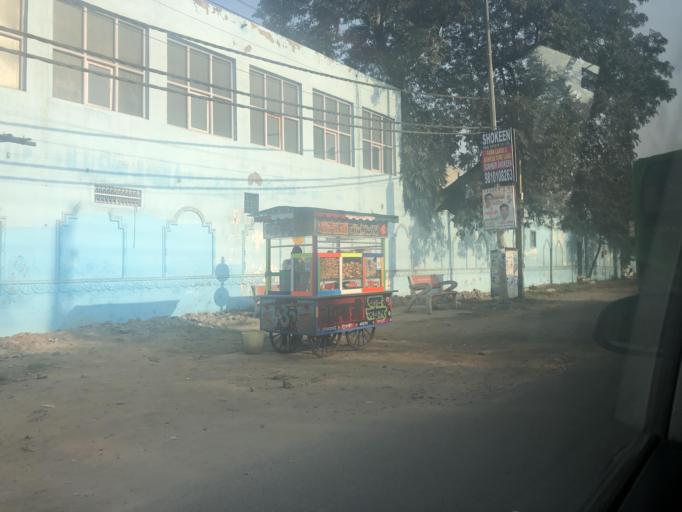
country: IN
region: Haryana
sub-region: Gurgaon
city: Gurgaon
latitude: 28.5579
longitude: 77.0044
